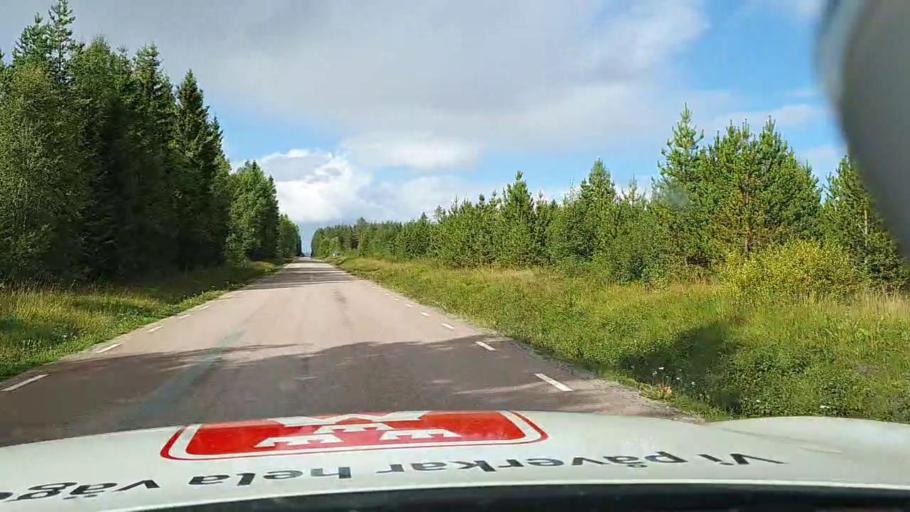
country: SE
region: Jaemtland
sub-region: Stroemsunds Kommun
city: Stroemsund
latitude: 63.8641
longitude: 15.3824
